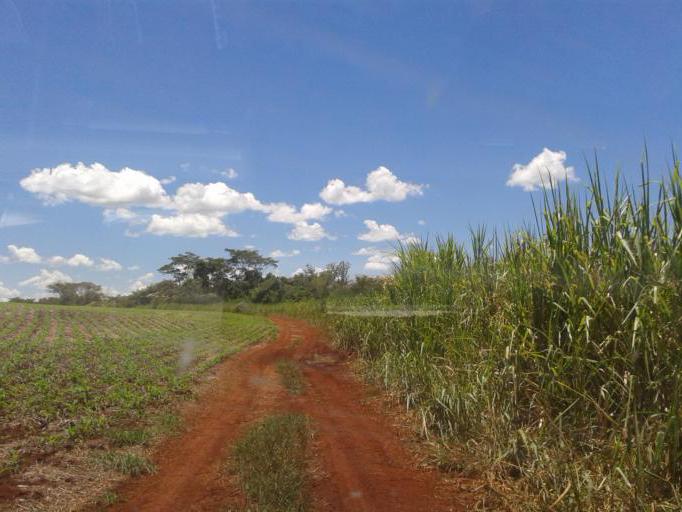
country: BR
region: Minas Gerais
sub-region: Capinopolis
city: Capinopolis
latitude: -18.5879
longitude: -49.5392
